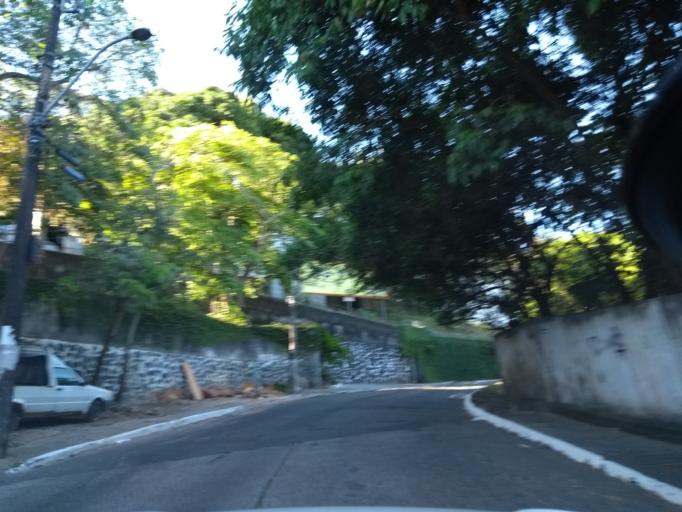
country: BR
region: Bahia
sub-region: Salvador
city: Salvador
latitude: -12.9930
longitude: -38.5141
